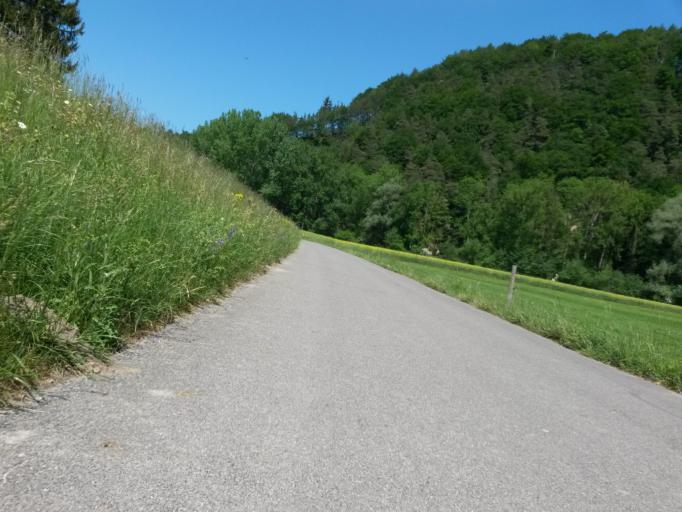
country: CH
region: Bern
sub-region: Bern-Mittelland District
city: Muhleberg
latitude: 46.9674
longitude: 7.2512
